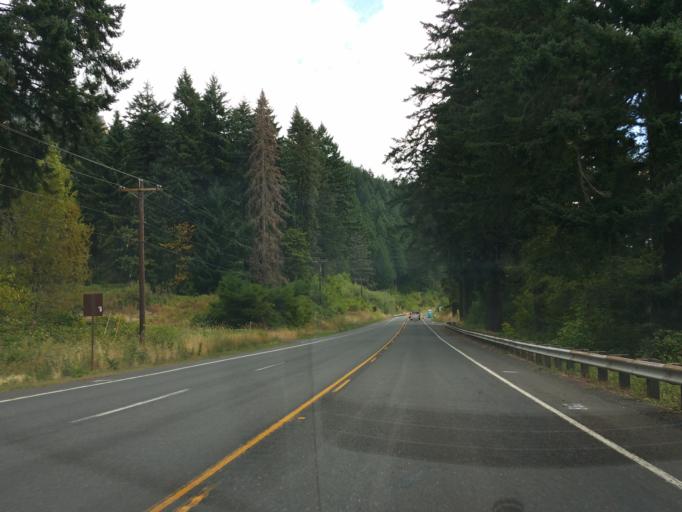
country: US
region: Oregon
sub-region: Hood River County
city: Cascade Locks
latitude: 45.6003
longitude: -122.1136
